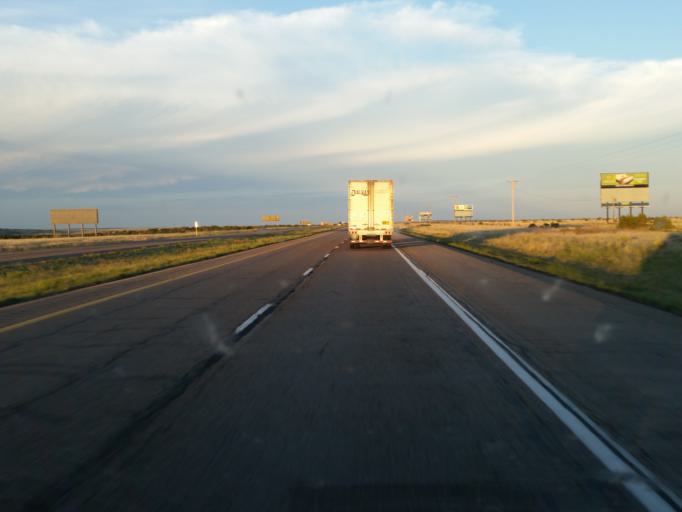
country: US
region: New Mexico
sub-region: San Miguel County
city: Las Vegas
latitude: 34.9941
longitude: -105.3496
